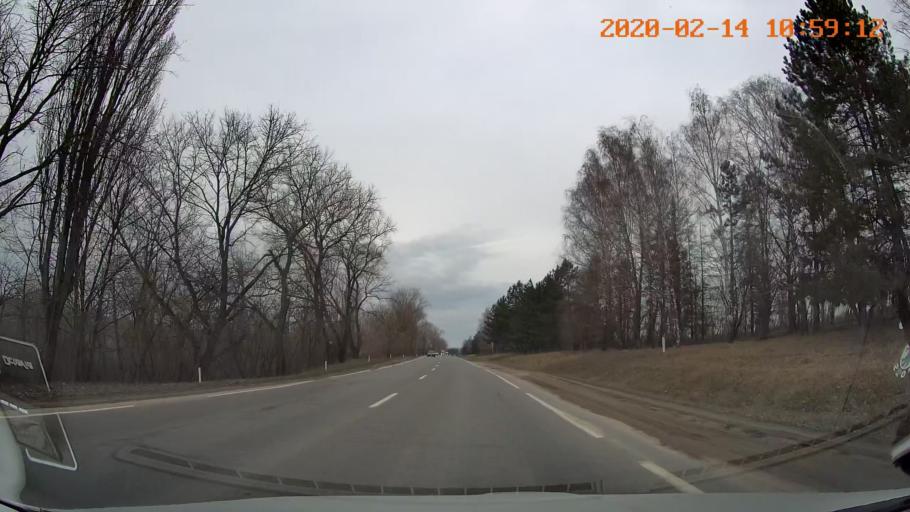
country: MD
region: Raionul Edinet
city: Edinet
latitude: 48.1401
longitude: 27.3550
